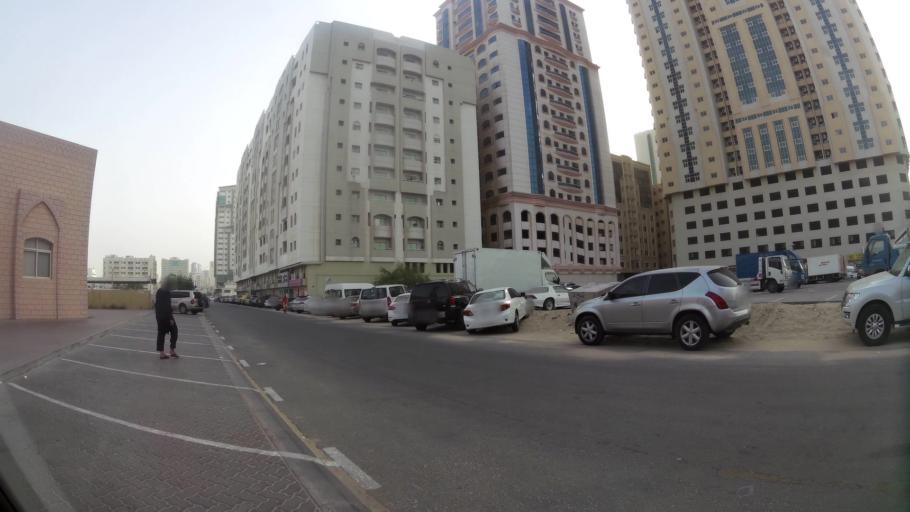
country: AE
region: Ash Shariqah
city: Sharjah
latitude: 25.3435
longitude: 55.4030
